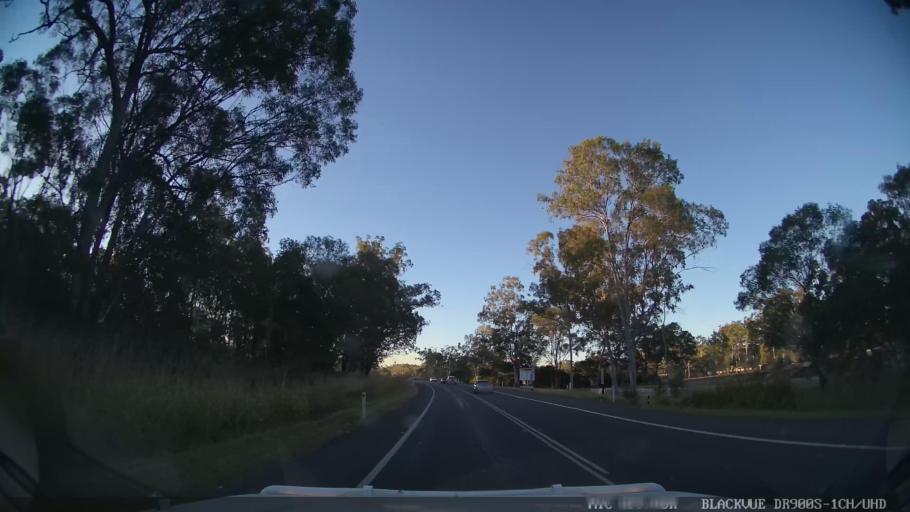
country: AU
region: Queensland
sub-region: Gladstone
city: Toolooa
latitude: -23.9565
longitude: 151.2199
